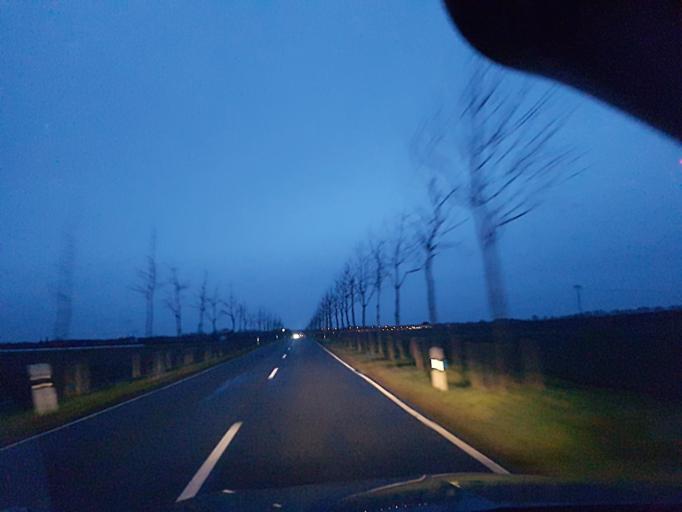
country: DE
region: Brandenburg
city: Doberlug-Kirchhain
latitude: 51.6165
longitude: 13.5785
